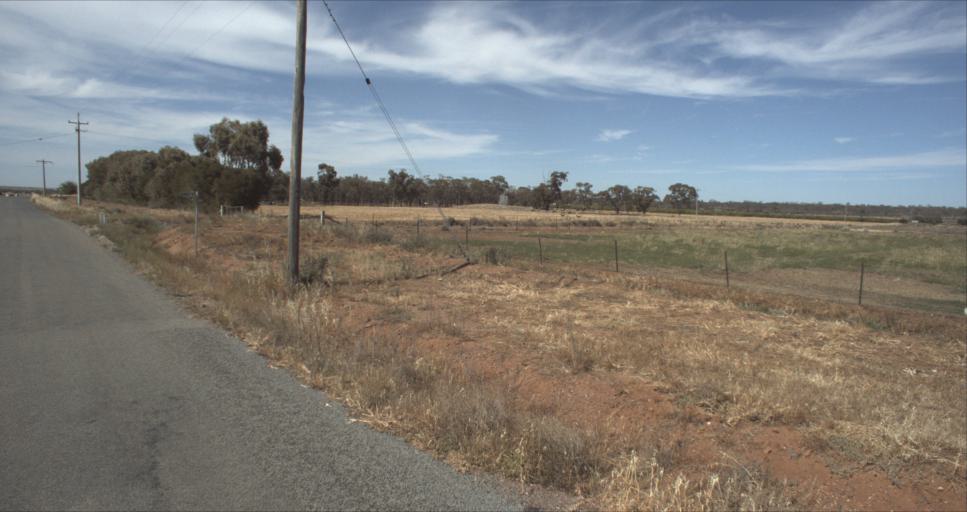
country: AU
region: New South Wales
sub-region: Leeton
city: Leeton
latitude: -34.5730
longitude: 146.4667
